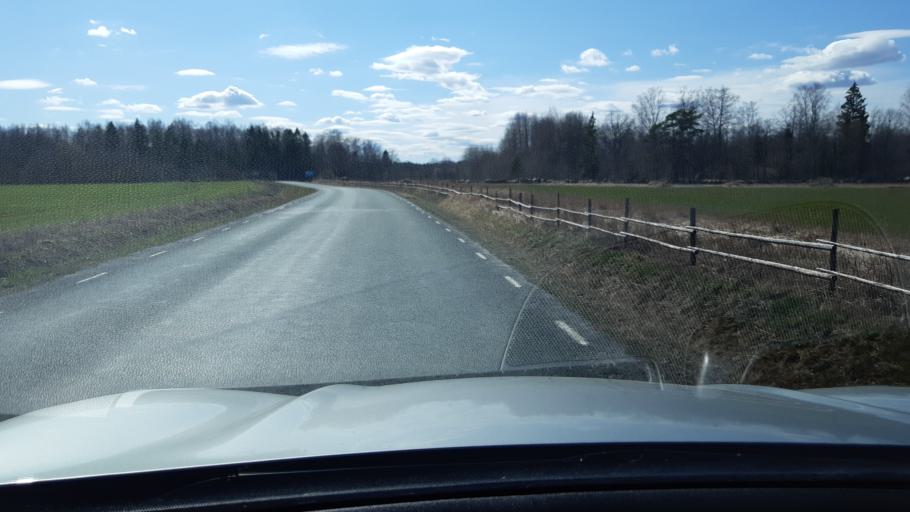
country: EE
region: Harju
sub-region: Rae vald
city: Vaida
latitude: 59.1993
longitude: 24.9055
